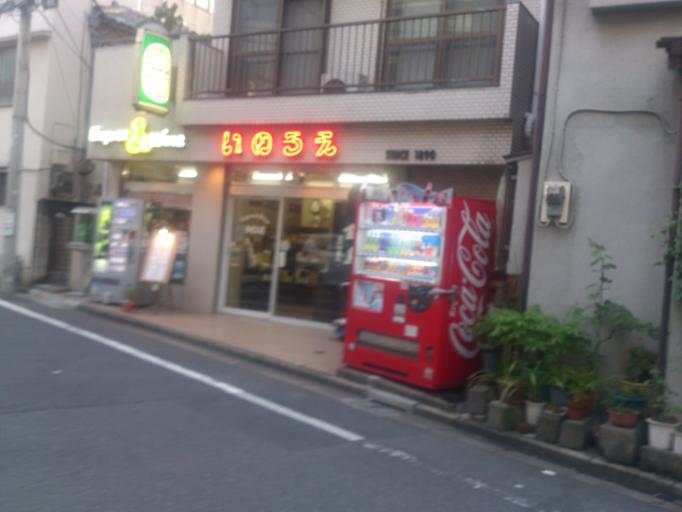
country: JP
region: Tokyo
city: Tokyo
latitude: 35.7102
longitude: 139.7240
